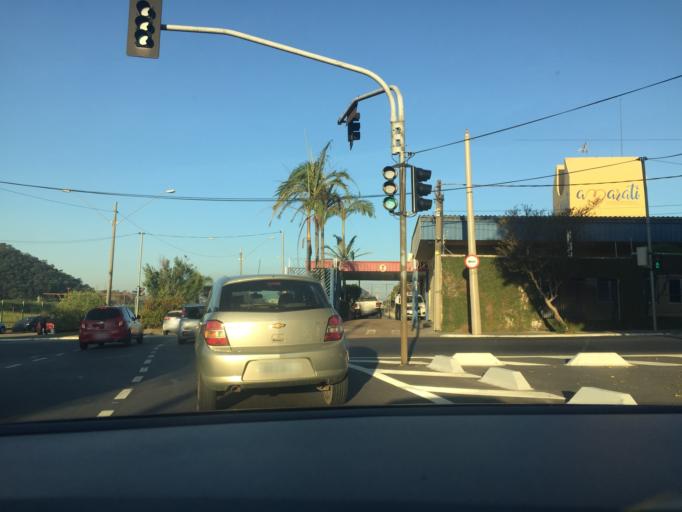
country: BR
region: Sao Paulo
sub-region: Jundiai
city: Jundiai
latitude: -23.2015
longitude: -46.8667
